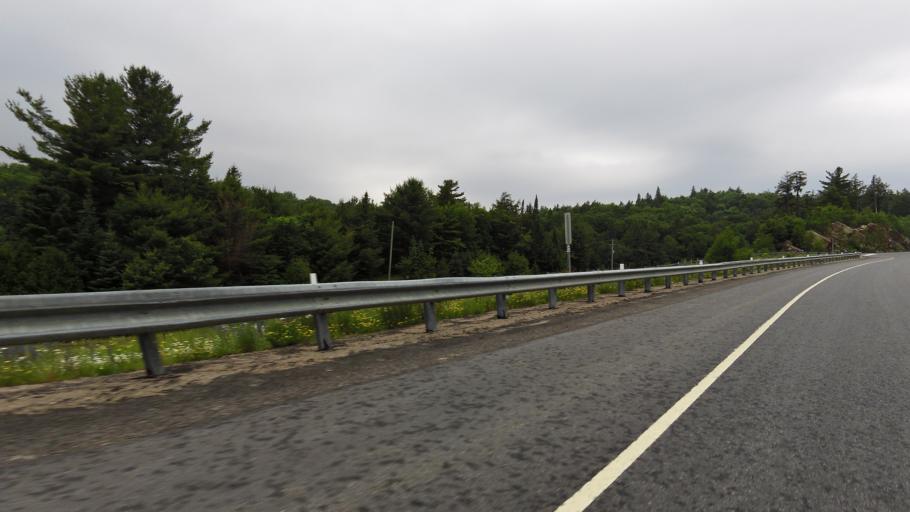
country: CA
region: Ontario
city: Huntsville
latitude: 45.5166
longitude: -78.7175
